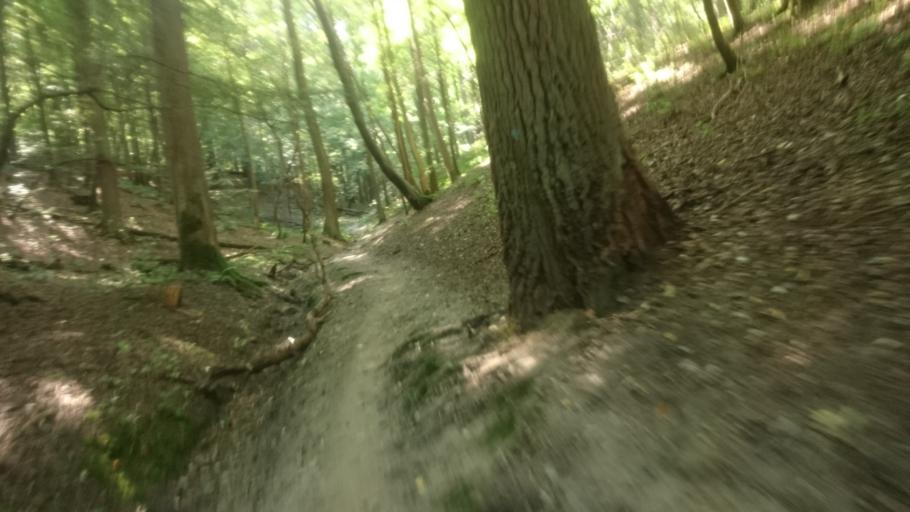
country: BE
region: Flanders
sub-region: Provincie Vlaams-Brabant
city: Hoeilaart
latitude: 50.8000
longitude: 4.4436
